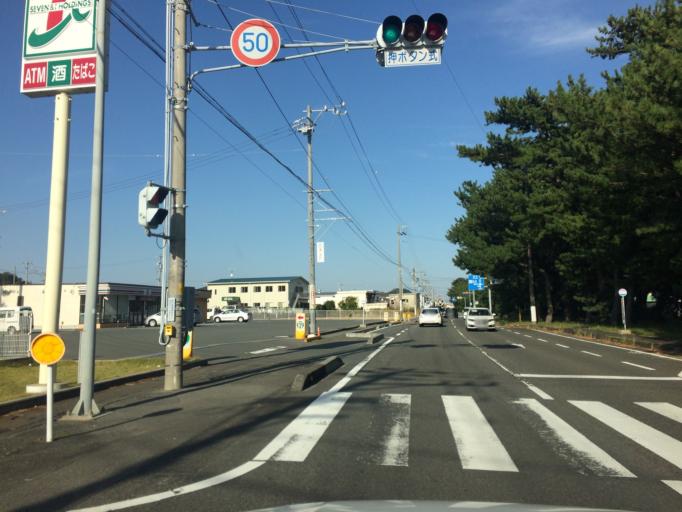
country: JP
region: Shizuoka
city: Sagara
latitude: 34.6756
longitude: 138.1981
